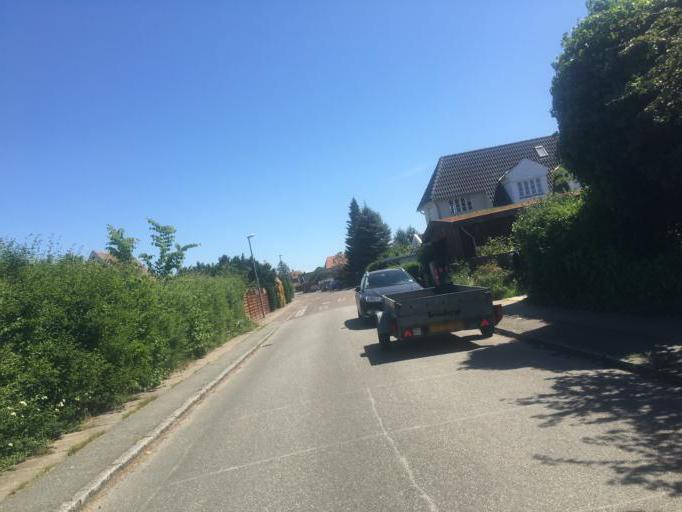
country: DK
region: Capital Region
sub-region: Tarnby Kommune
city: Tarnby
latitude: 55.6261
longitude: 12.6188
